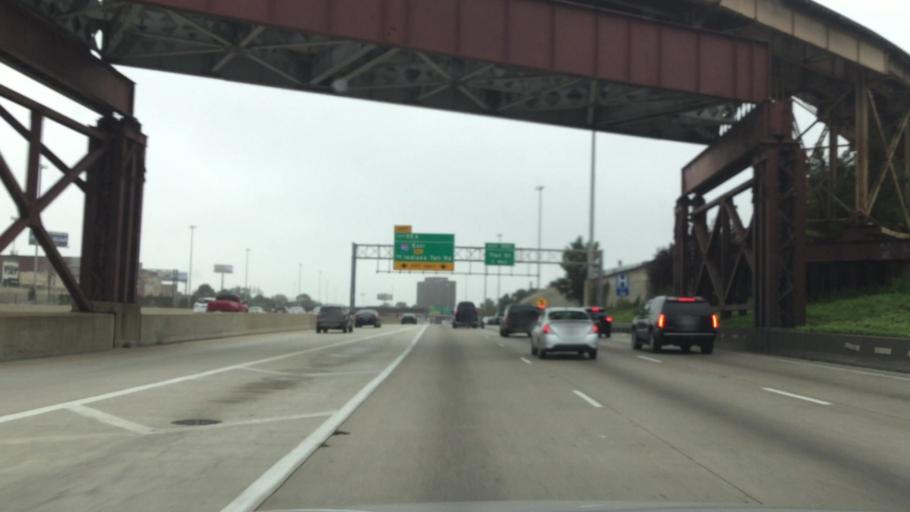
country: US
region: Illinois
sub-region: Cook County
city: Chicago
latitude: 41.7869
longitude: -87.6316
